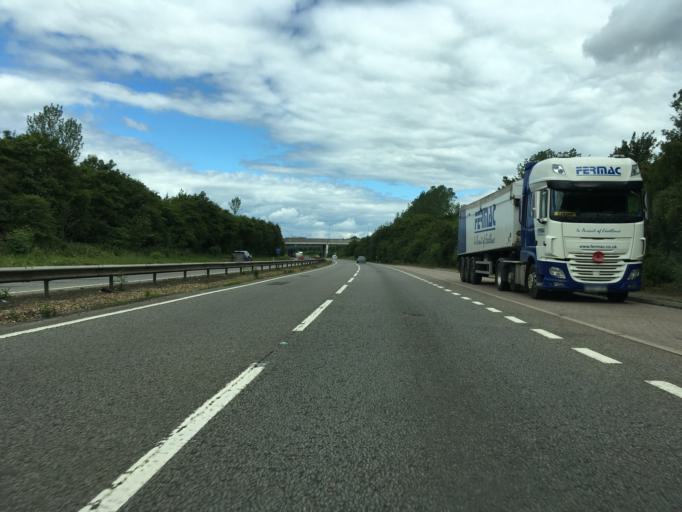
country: GB
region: England
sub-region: Milton Keynes
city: Milton Keynes
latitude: 52.0204
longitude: -0.7588
